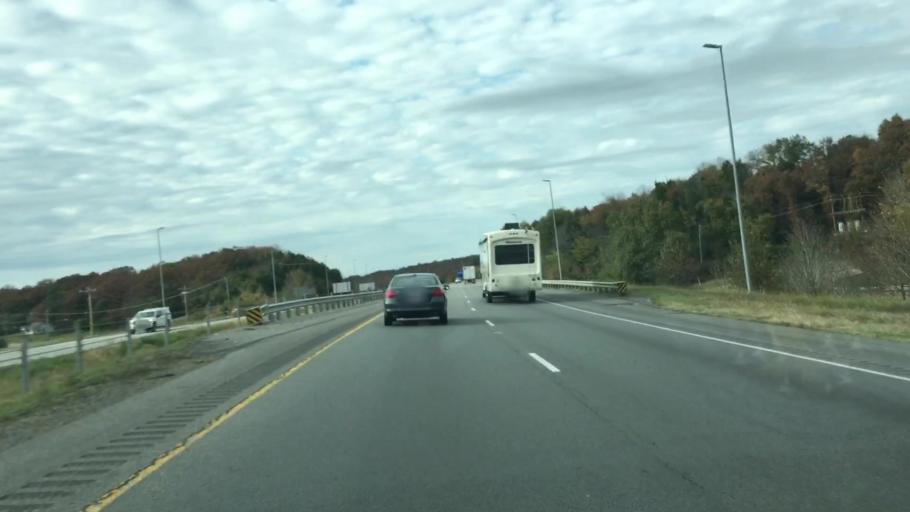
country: US
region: Arkansas
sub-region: Faulkner County
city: Conway
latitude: 35.1149
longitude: -92.4469
